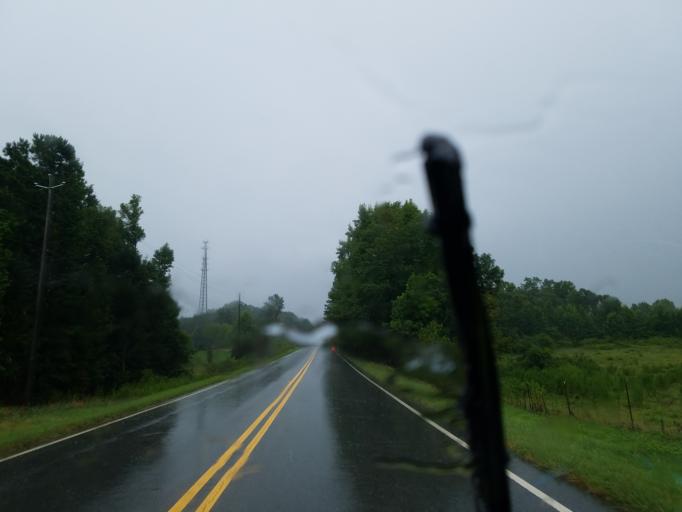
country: US
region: Georgia
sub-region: Floyd County
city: Shannon
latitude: 34.3693
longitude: -85.0634
